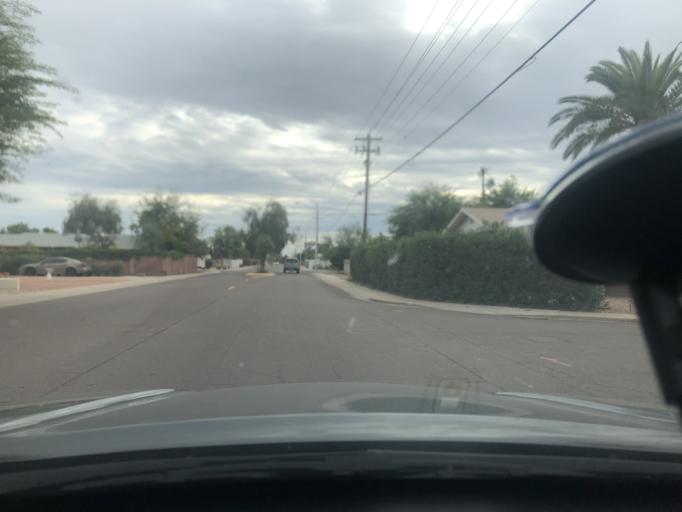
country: US
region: Arizona
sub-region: Maricopa County
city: Scottsdale
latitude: 33.4942
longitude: -111.9046
